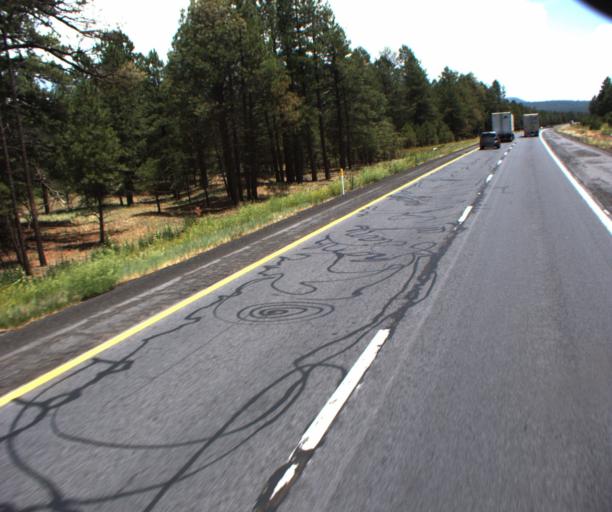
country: US
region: Arizona
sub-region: Coconino County
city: Parks
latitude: 35.2480
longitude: -111.8560
